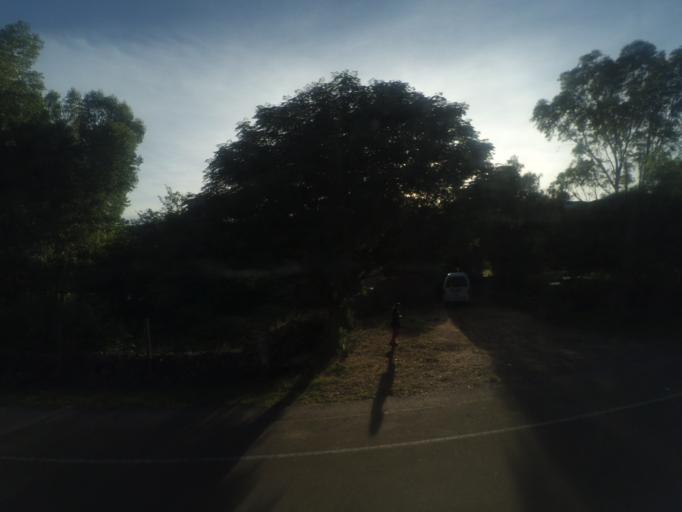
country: BO
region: Tarija
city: Tarija
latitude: -21.5248
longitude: -64.5745
